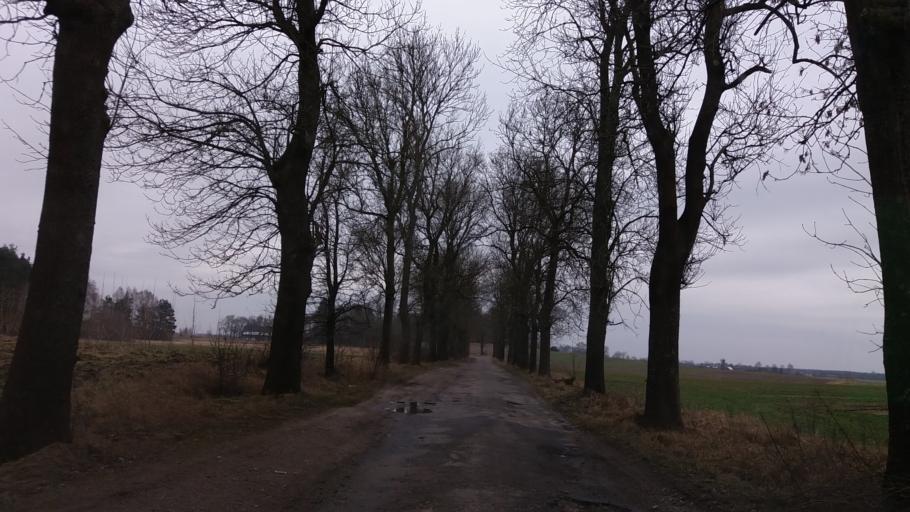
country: PL
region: Lubusz
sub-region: Powiat strzelecko-drezdenecki
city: Dobiegniew
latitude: 53.0254
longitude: 15.7363
